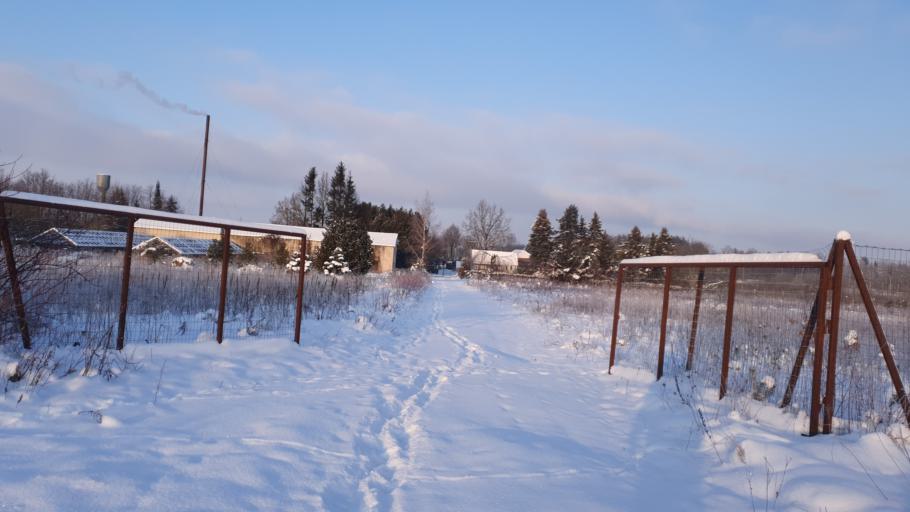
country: LT
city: Skaidiskes
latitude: 54.6484
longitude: 25.4244
